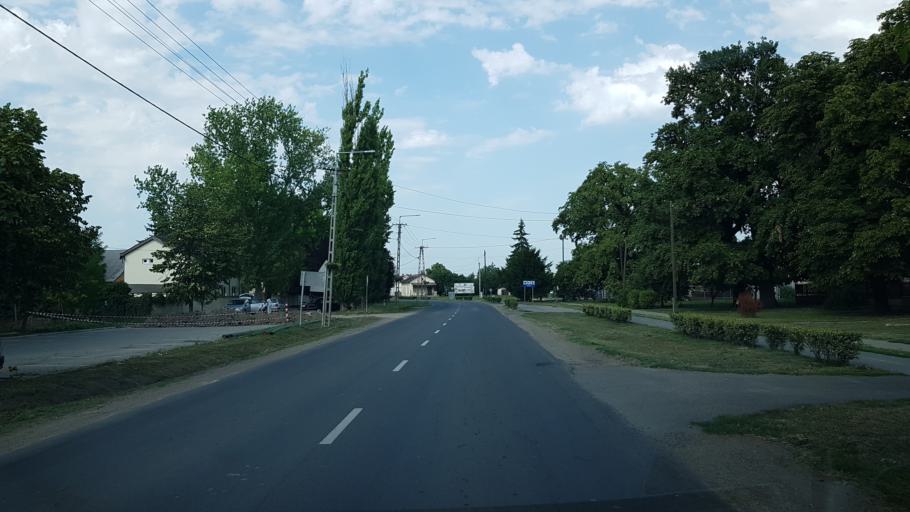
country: HU
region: Bekes
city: Fuzesgyarmat
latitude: 47.0957
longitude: 21.2064
